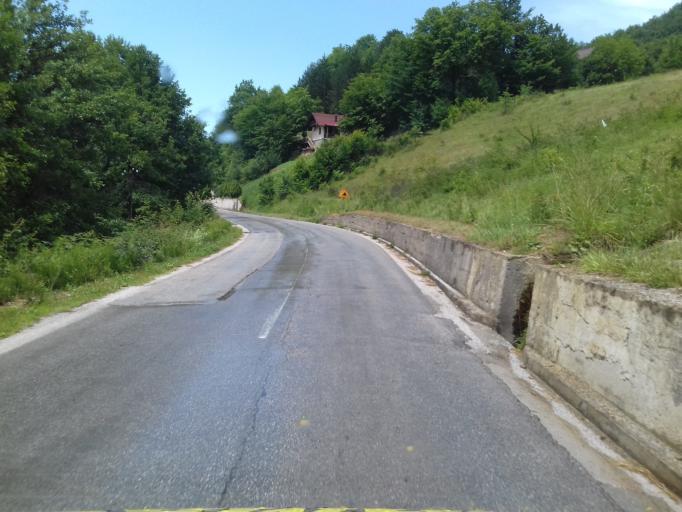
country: BA
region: Federation of Bosnia and Herzegovina
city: Kiseljak
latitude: 43.9502
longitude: 18.0942
